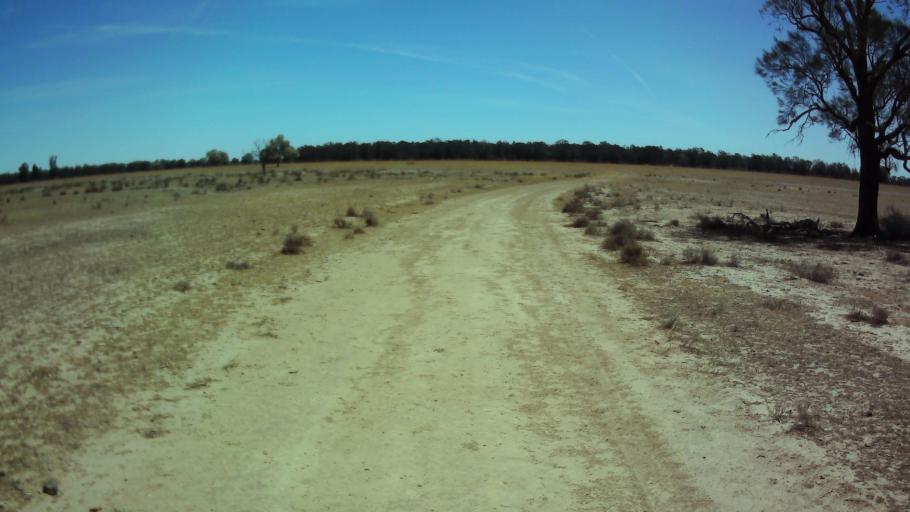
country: AU
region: New South Wales
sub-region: Bland
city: West Wyalong
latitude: -33.8385
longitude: 147.6318
